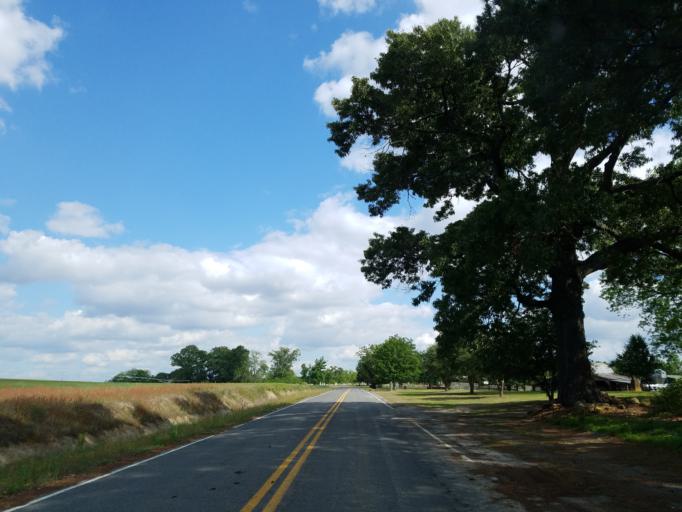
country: US
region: Georgia
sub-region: Dooly County
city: Unadilla
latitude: 32.2555
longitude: -83.7863
